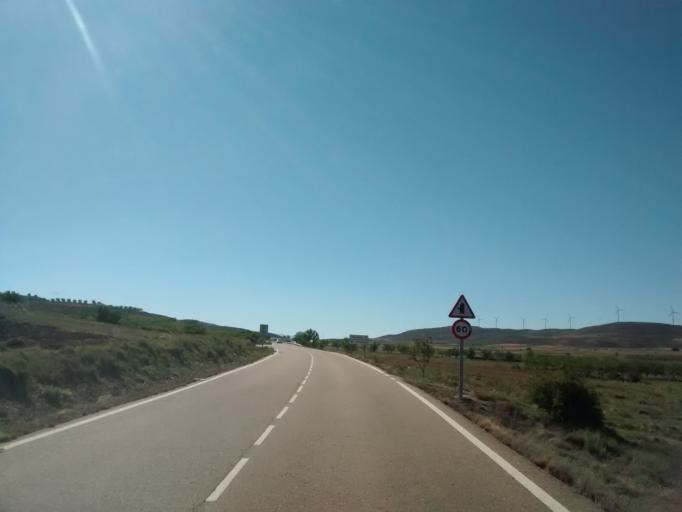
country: ES
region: Aragon
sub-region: Provincia de Zaragoza
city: Trasmoz
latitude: 41.8436
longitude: -1.7207
